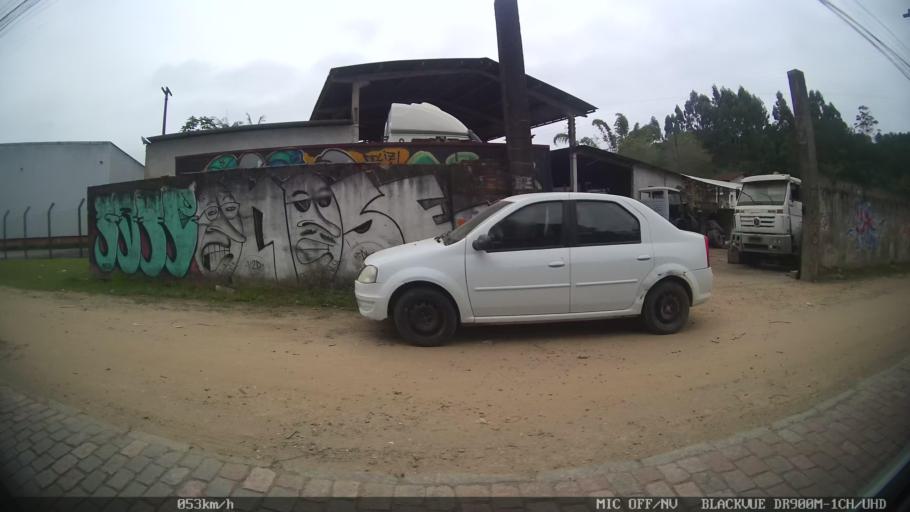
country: BR
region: Santa Catarina
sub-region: Joinville
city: Joinville
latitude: -26.3612
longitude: -48.8415
